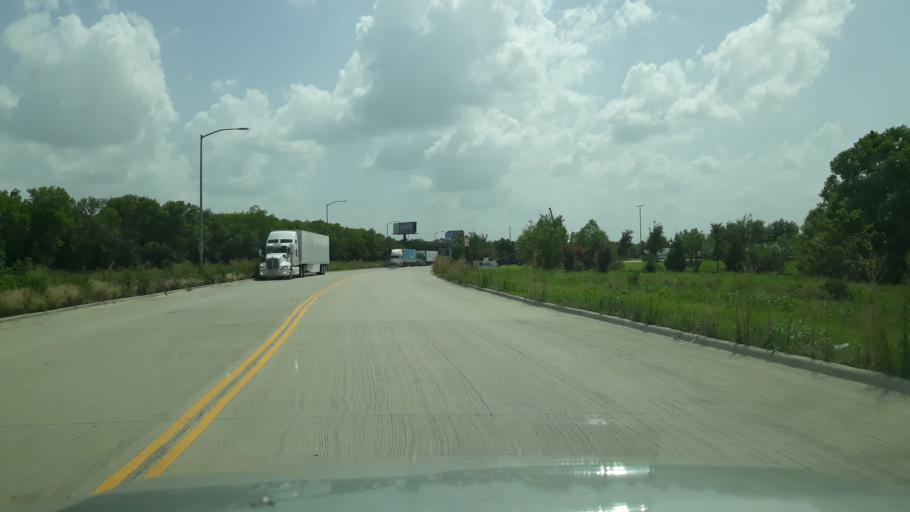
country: US
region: Texas
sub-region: Dallas County
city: Coppell
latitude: 32.9493
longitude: -97.0245
